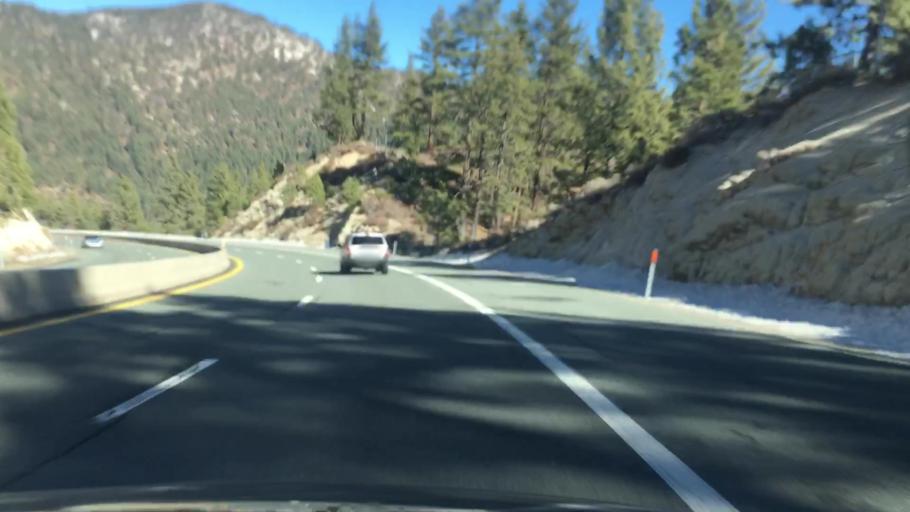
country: US
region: Nevada
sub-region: Douglas County
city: Indian Hills
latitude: 39.1078
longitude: -119.8791
